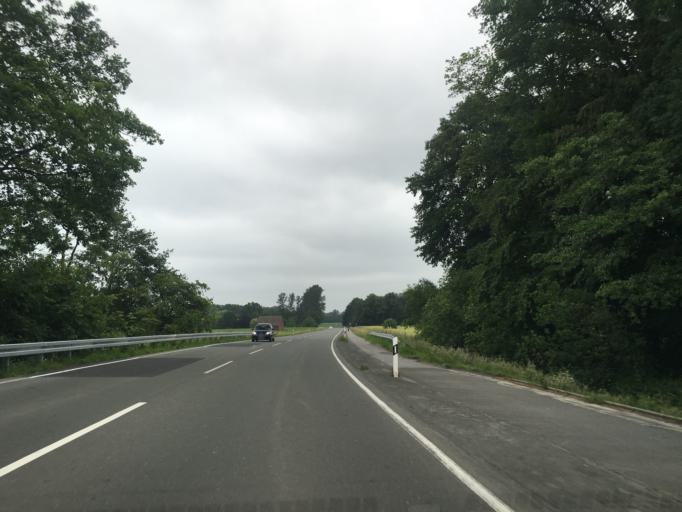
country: DE
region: North Rhine-Westphalia
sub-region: Regierungsbezirk Munster
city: Steinfurt
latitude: 52.1164
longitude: 7.3356
